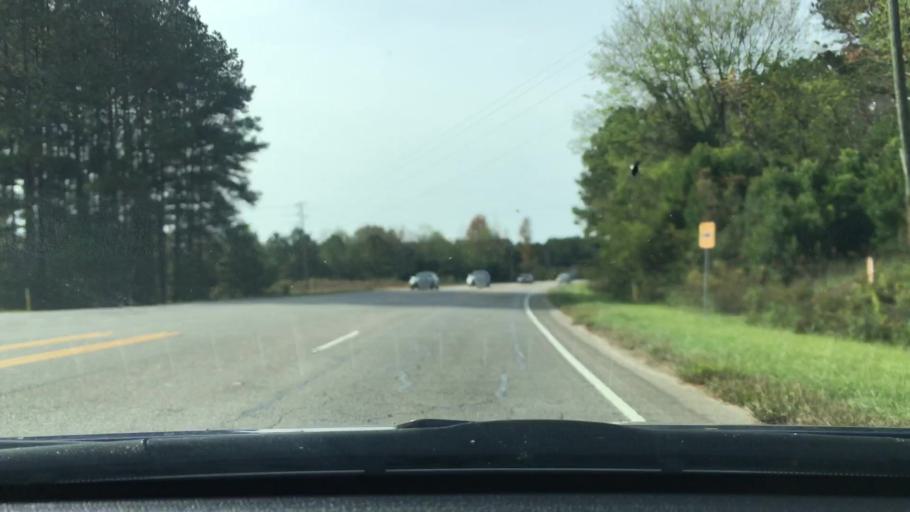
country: US
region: South Carolina
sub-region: Sumter County
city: Cherryvale
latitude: 33.9363
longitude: -80.4420
